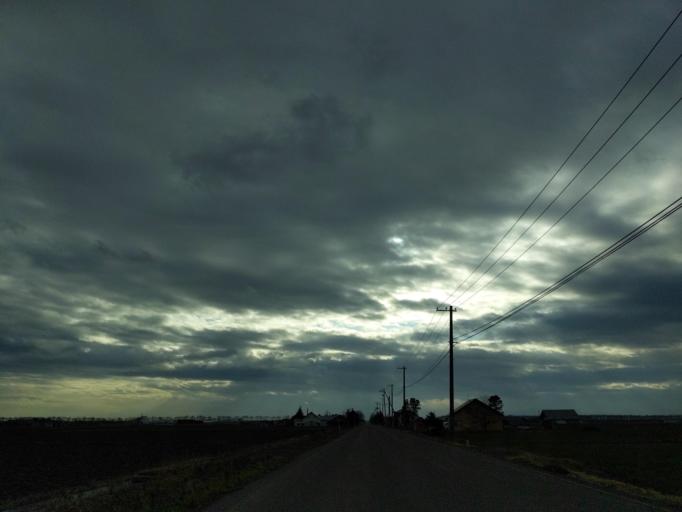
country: JP
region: Hokkaido
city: Kitahiroshima
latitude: 43.0161
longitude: 141.6736
